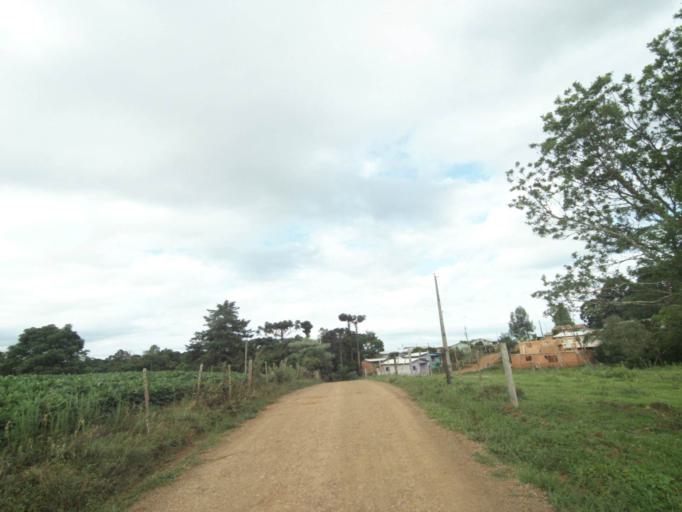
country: BR
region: Rio Grande do Sul
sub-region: Lagoa Vermelha
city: Lagoa Vermelha
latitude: -28.2026
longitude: -51.5092
